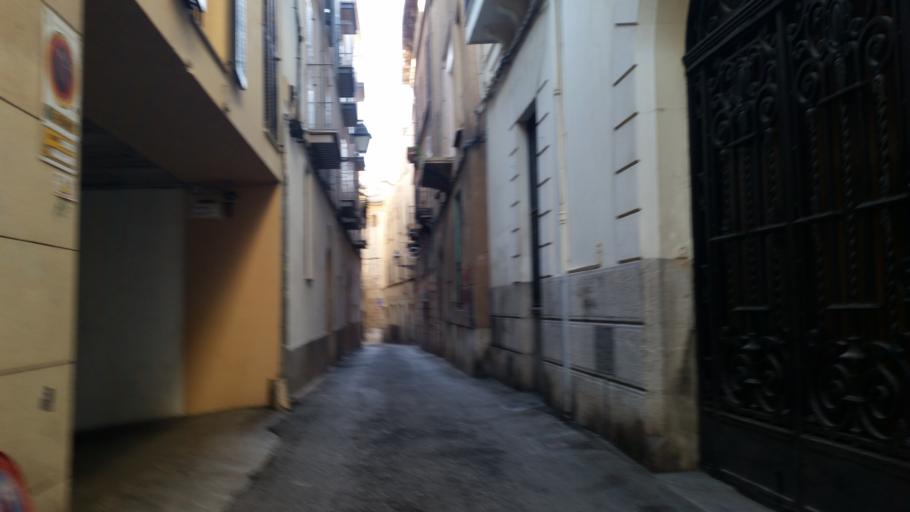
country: ES
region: Balearic Islands
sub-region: Illes Balears
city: Palma
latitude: 39.5728
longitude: 2.6467
